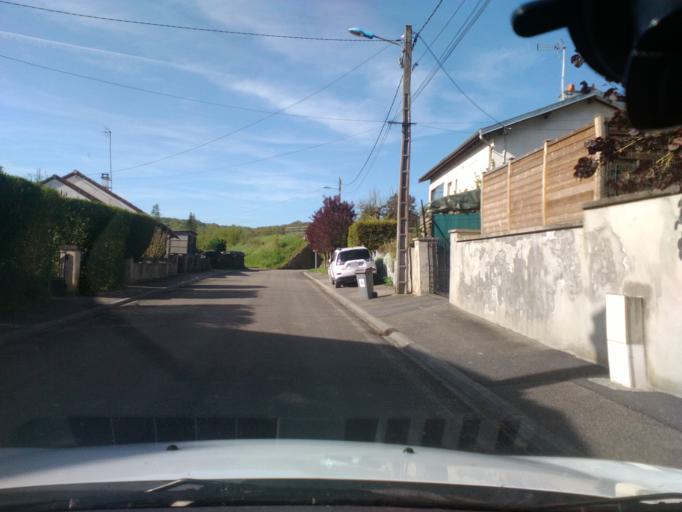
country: FR
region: Lorraine
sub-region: Departement des Vosges
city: Mirecourt
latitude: 48.2781
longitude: 6.1316
